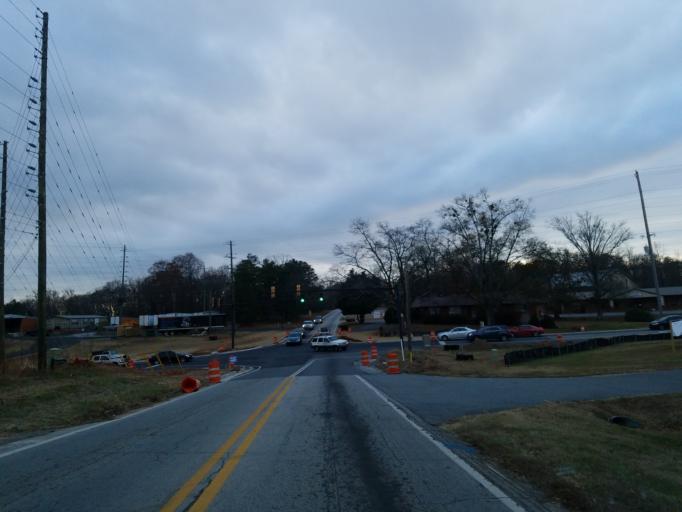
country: US
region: Georgia
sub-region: Dawson County
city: Dawsonville
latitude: 34.3679
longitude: -84.0404
